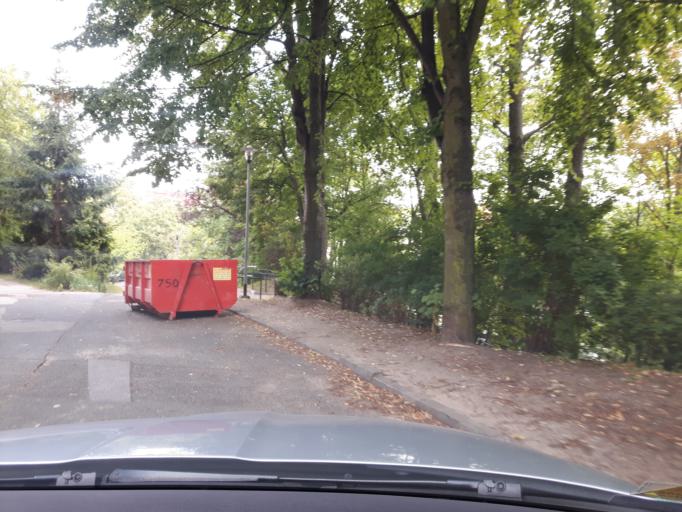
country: PL
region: Pomeranian Voivodeship
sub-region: Gdynia
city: Gdynia
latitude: 54.5068
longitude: 18.5393
